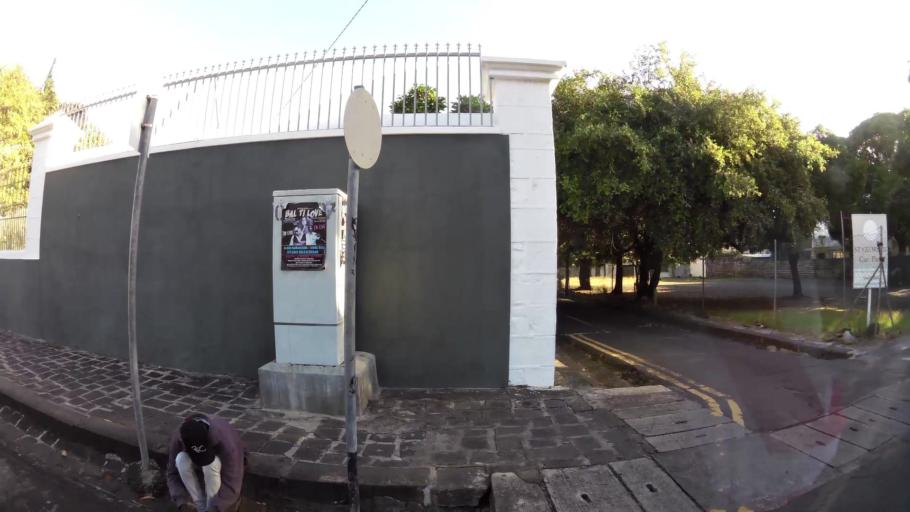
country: MU
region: Port Louis
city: Port Louis
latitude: -20.1669
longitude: 57.5016
